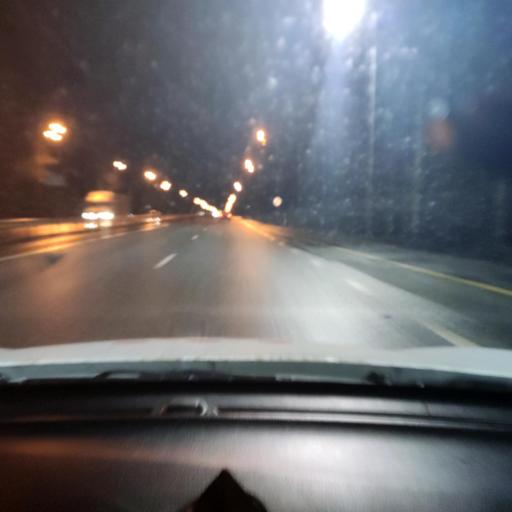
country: RU
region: Tatarstan
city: Osinovo
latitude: 55.8409
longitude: 48.8516
